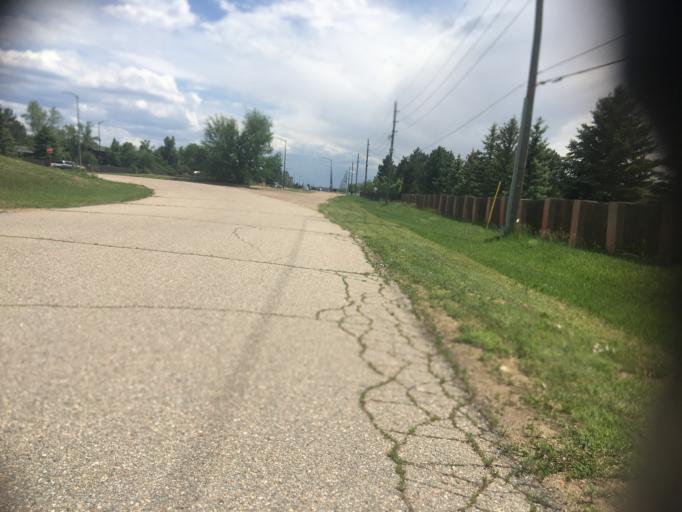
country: US
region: Colorado
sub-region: Boulder County
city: Superior
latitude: 39.9848
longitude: -105.1660
